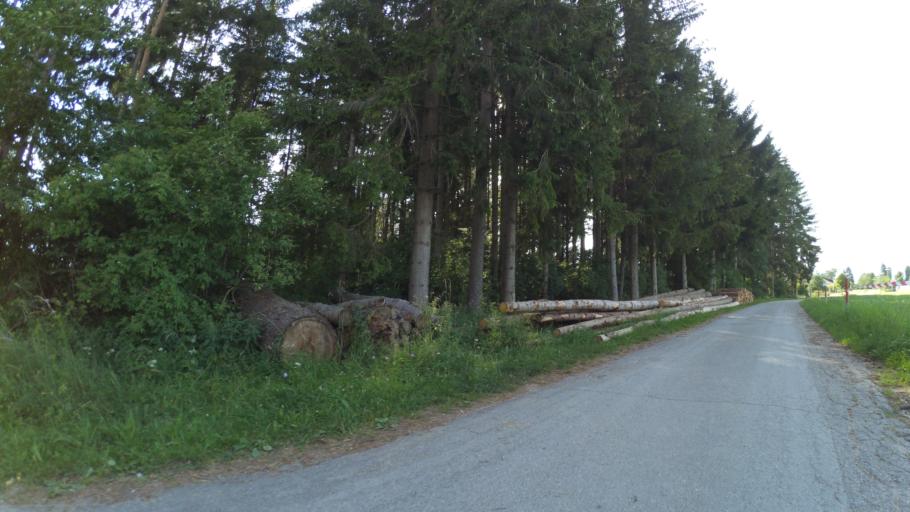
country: DE
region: Baden-Wuerttemberg
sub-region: Freiburg Region
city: Loffingen
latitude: 47.8548
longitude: 8.4094
